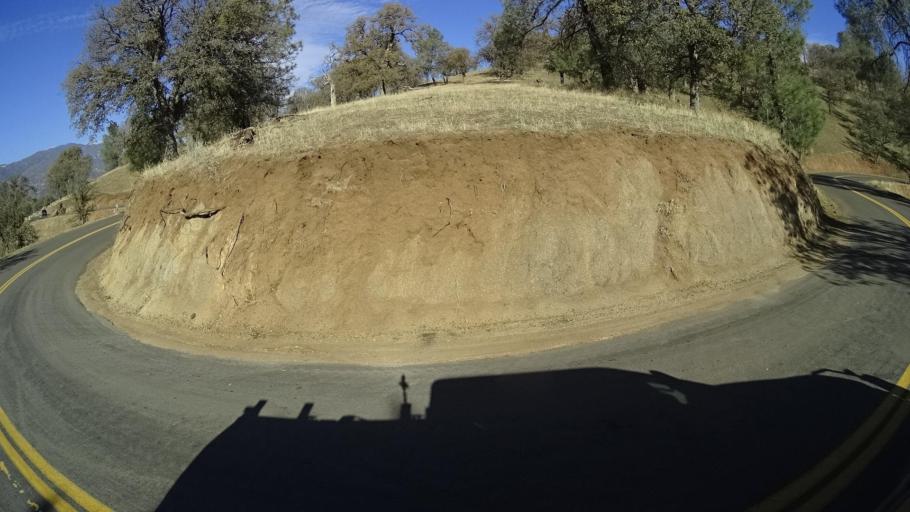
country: US
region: California
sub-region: Kern County
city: Bear Valley Springs
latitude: 35.3637
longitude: -118.5533
